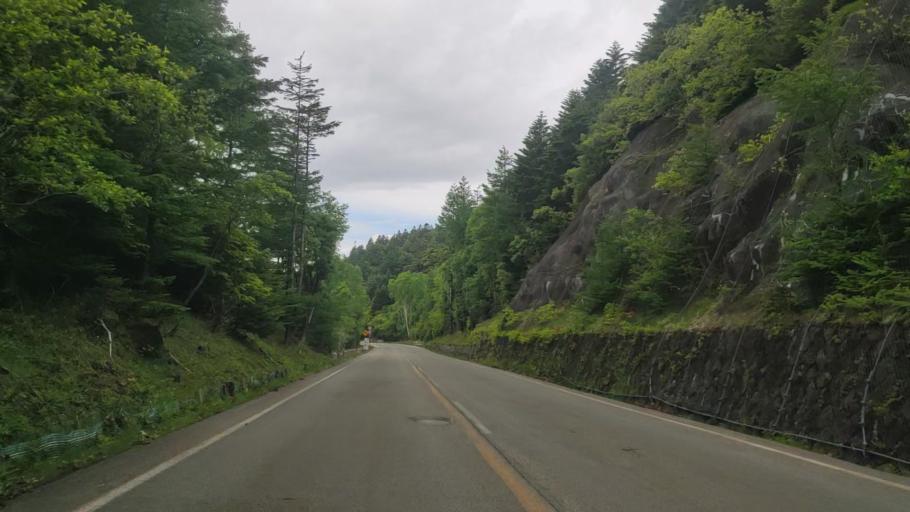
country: JP
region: Yamanashi
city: Fujikawaguchiko
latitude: 35.3816
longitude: 138.6906
